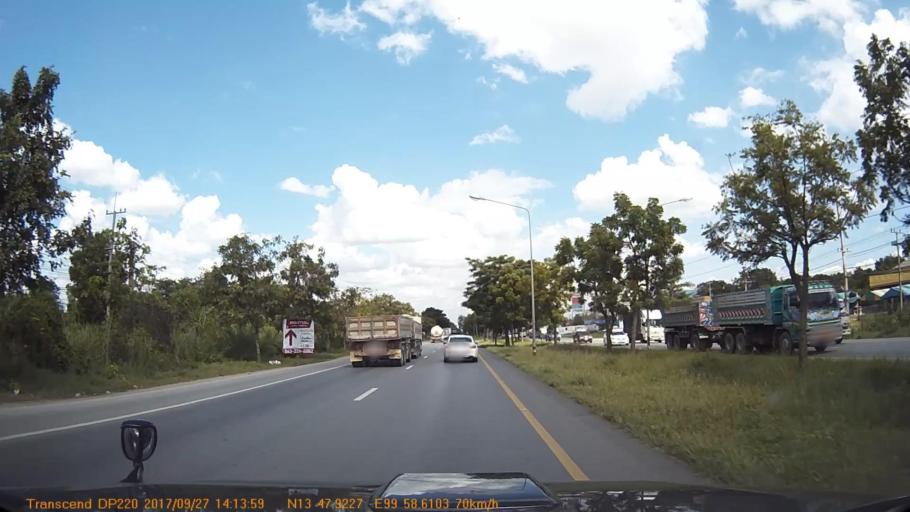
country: TH
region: Nakhon Pathom
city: Nakhon Pathom
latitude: 13.7987
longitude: 99.9769
